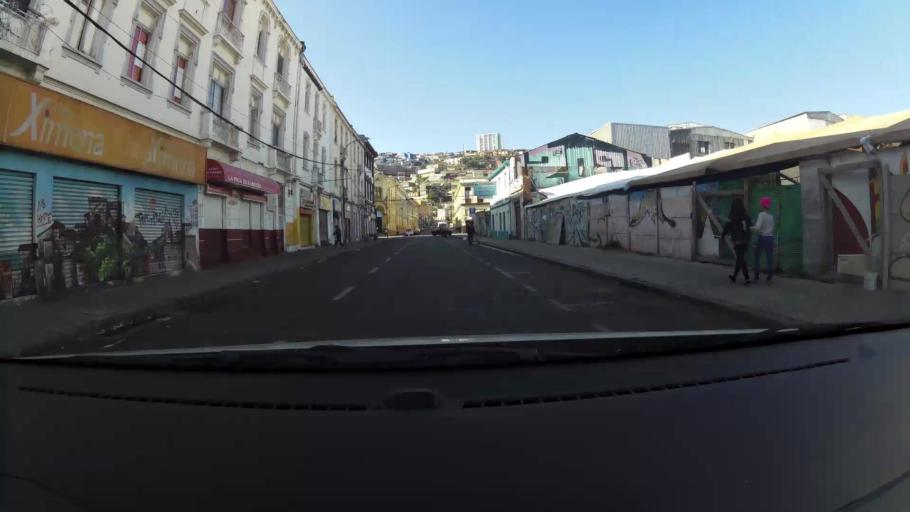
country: CL
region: Valparaiso
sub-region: Provincia de Valparaiso
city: Valparaiso
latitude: -33.0472
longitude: -71.6162
